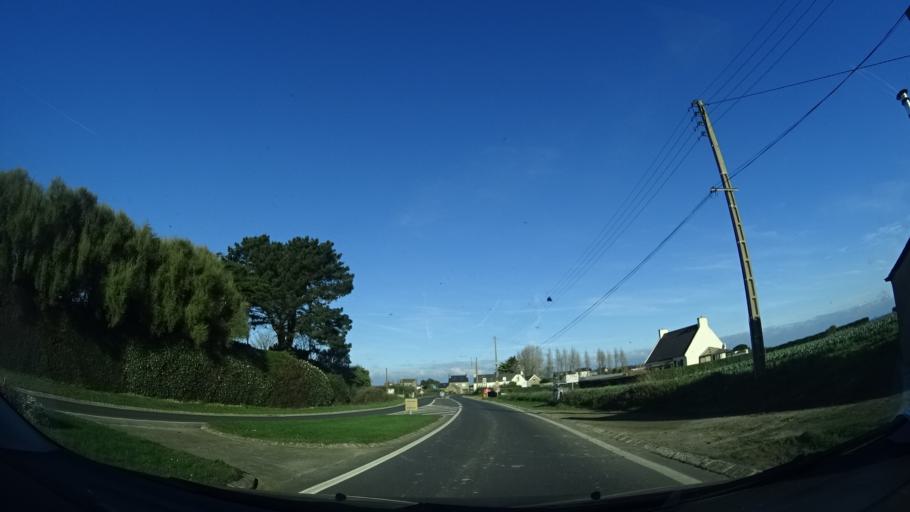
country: FR
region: Brittany
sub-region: Departement du Finistere
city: Roscoff
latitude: 48.7044
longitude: -3.9864
